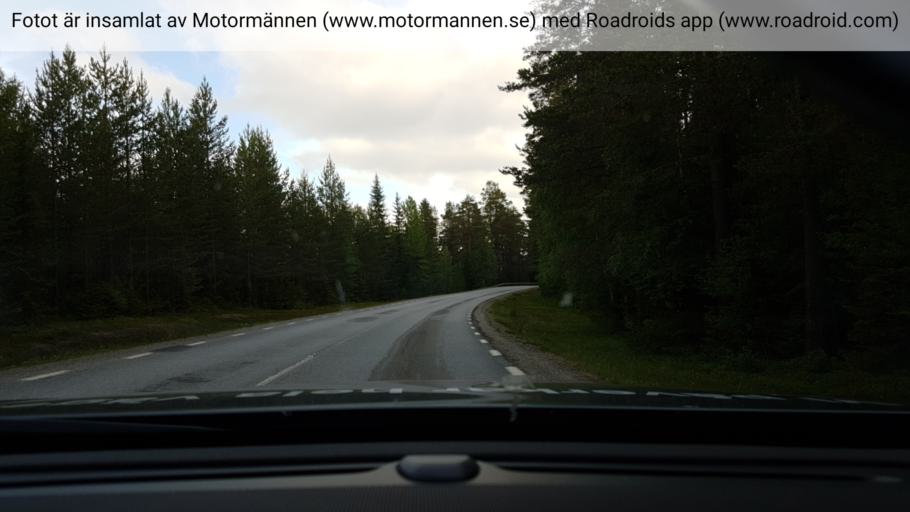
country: SE
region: Vaesterbotten
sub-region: Vindelns Kommun
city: Vindeln
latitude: 64.2591
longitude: 19.6303
